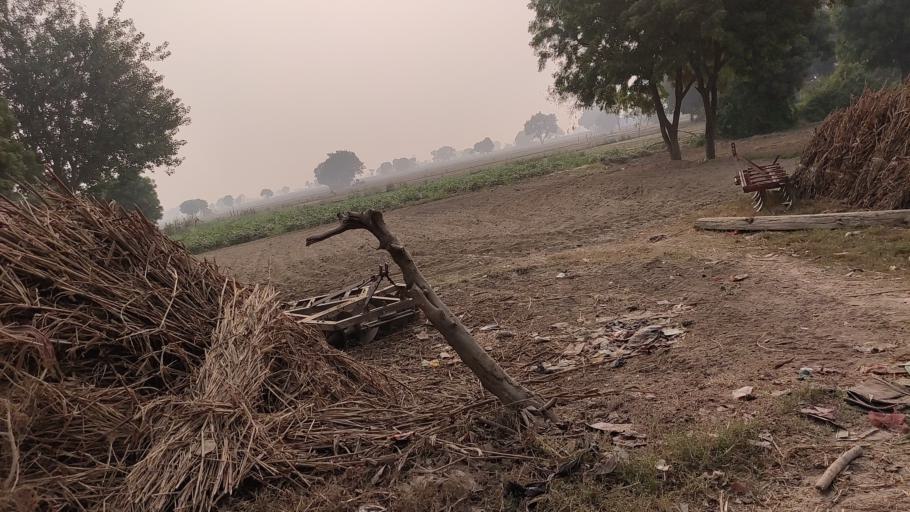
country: IN
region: Uttar Pradesh
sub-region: Mathura
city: Vrindavan
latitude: 27.5445
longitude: 77.7107
